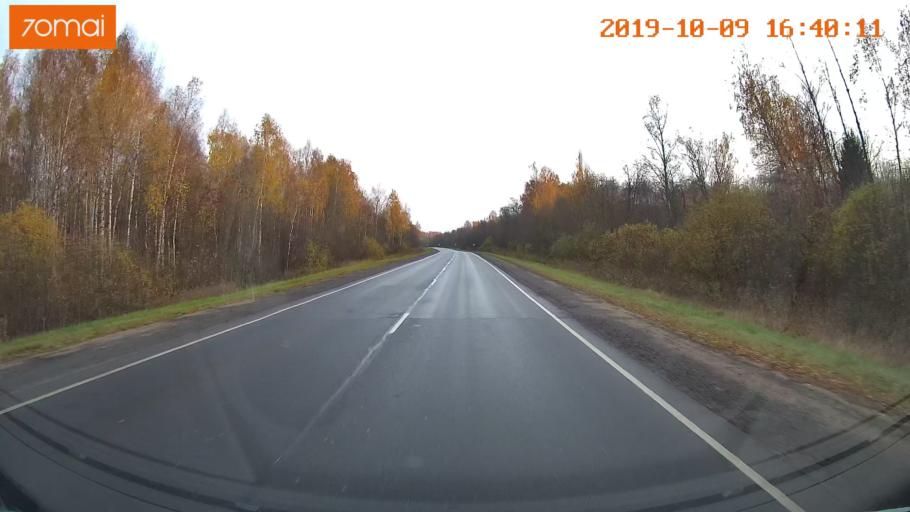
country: RU
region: Kostroma
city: Volgorechensk
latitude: 57.4871
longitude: 41.0575
